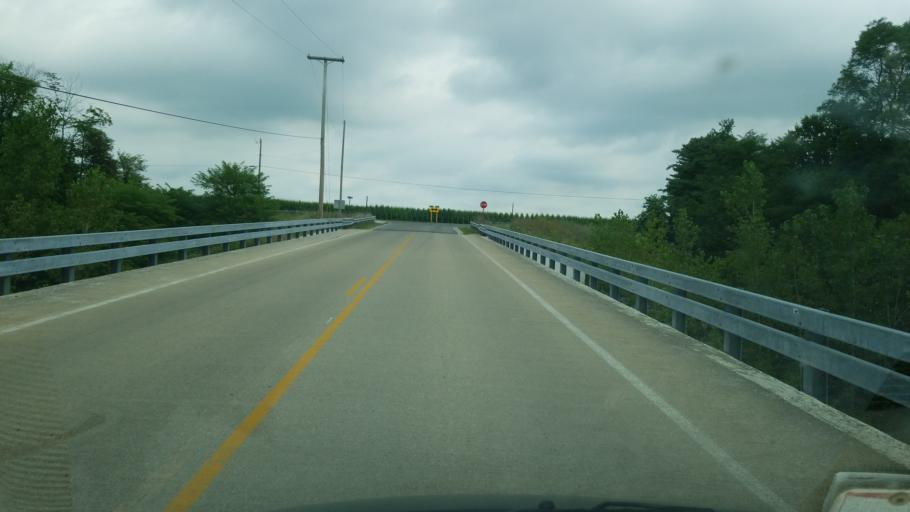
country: US
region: Ohio
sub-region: Seneca County
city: Tiffin
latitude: 41.2099
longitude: -83.1463
